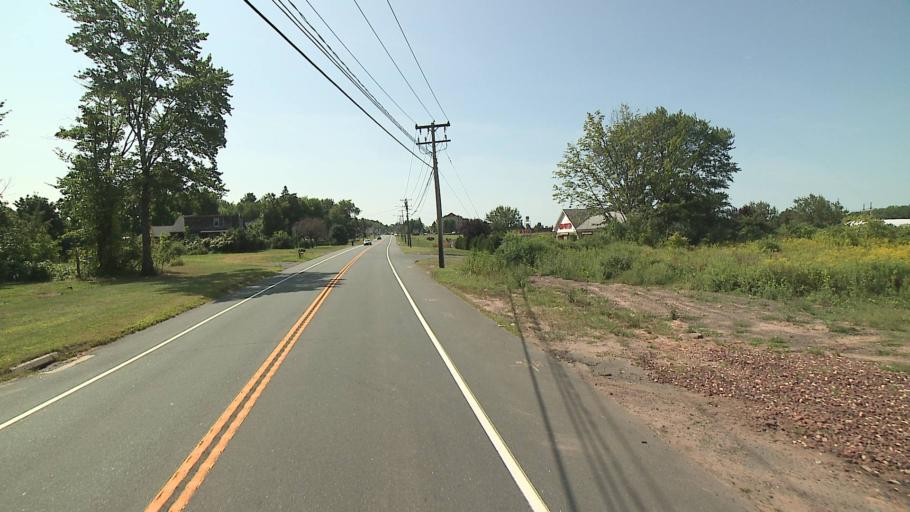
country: US
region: Connecticut
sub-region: Hartford County
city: Windsor Locks
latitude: 41.9350
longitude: -72.6041
